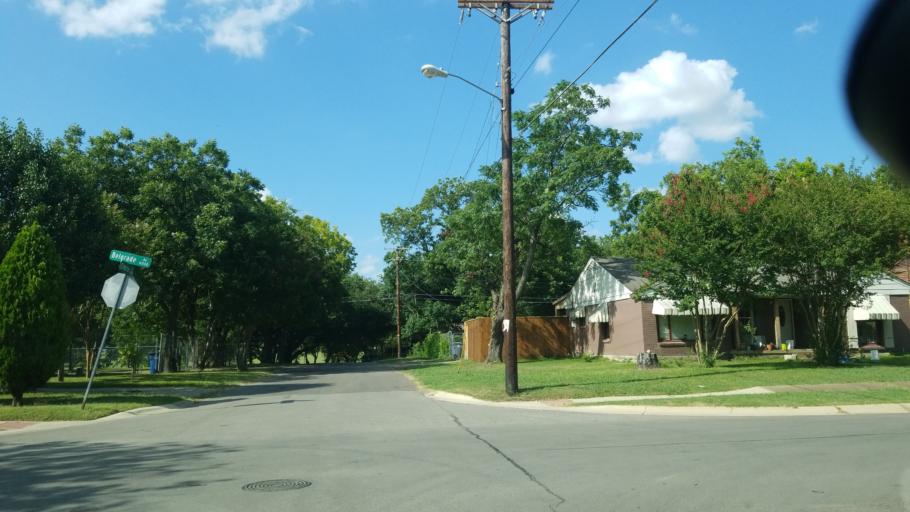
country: US
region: Texas
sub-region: Dallas County
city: Dallas
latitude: 32.7738
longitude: -96.7151
